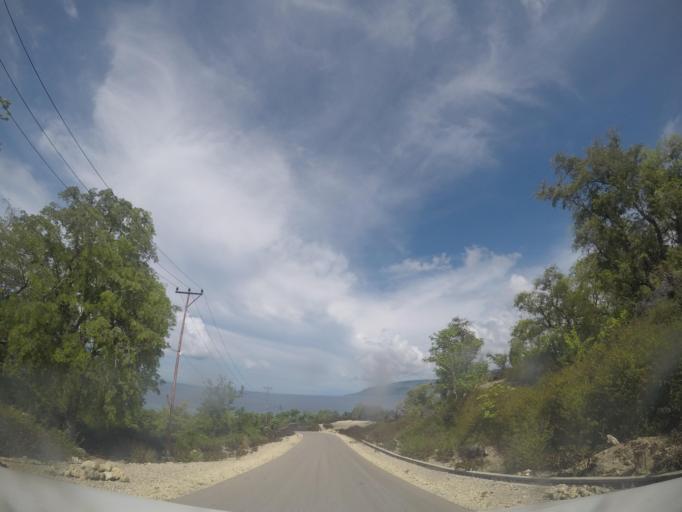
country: TL
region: Lautem
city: Lospalos
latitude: -8.3600
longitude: 127.0557
